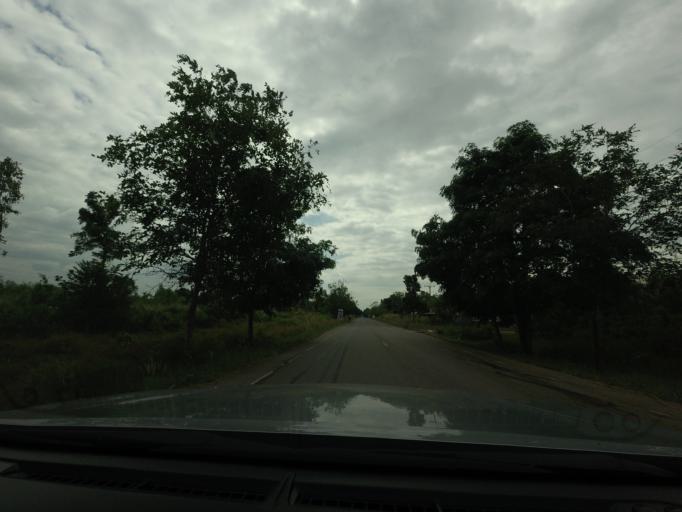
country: TH
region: Phitsanulok
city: Noen Maprang
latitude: 16.6224
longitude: 100.6188
